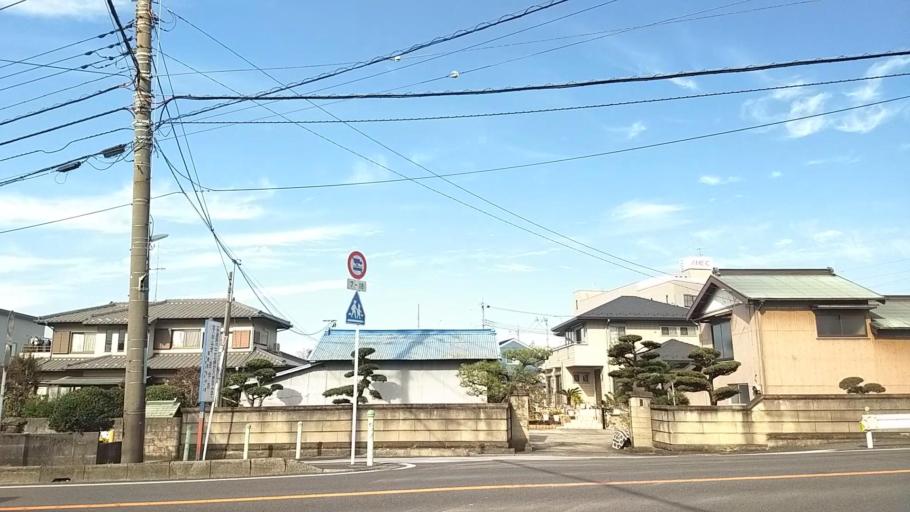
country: JP
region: Kanagawa
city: Zama
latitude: 35.4625
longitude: 139.3887
